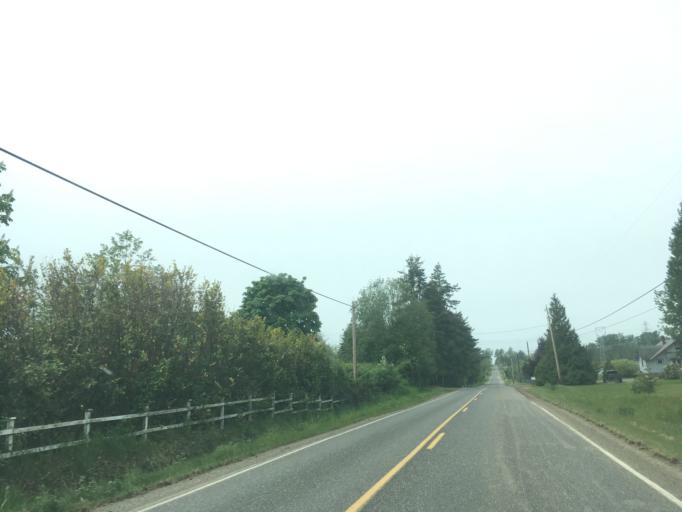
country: US
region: Washington
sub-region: Whatcom County
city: Bellingham
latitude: 48.8188
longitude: -122.4519
